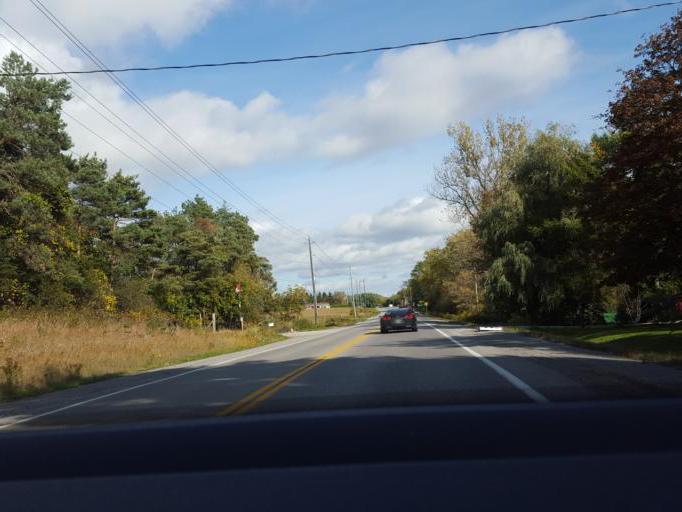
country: CA
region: Ontario
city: Oshawa
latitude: 43.9821
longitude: -78.6633
